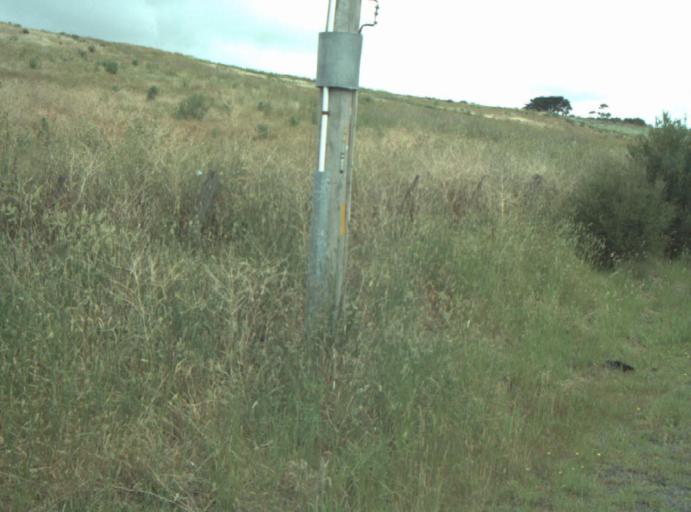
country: AU
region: Victoria
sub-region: Greater Geelong
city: Wandana Heights
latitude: -38.2041
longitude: 144.2707
